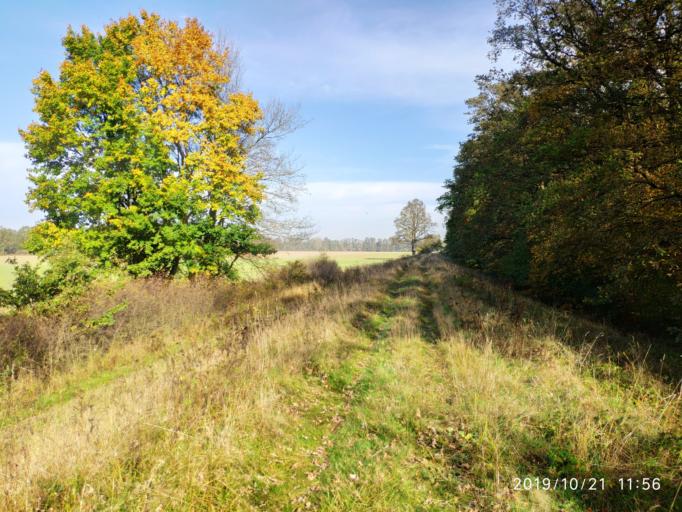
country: PL
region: Lubusz
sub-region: Powiat nowosolski
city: Przyborow
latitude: 51.8626
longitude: 15.7725
